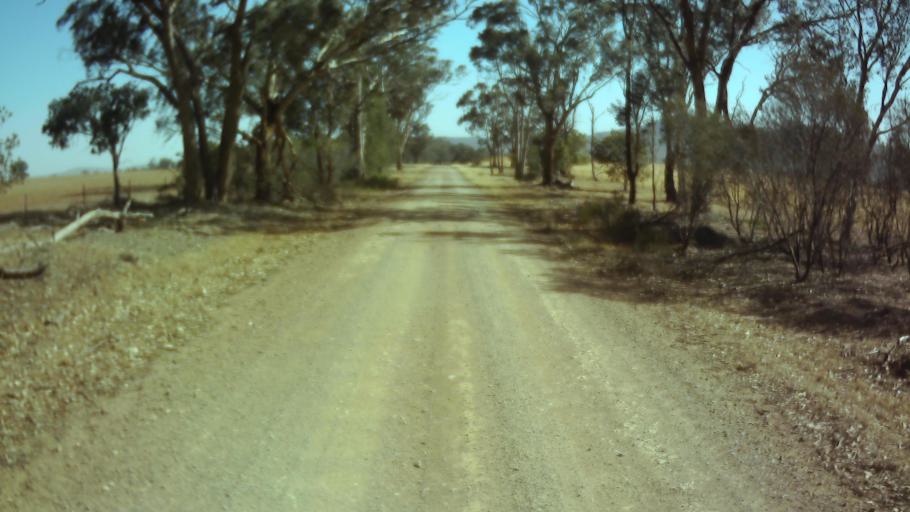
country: AU
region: New South Wales
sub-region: Weddin
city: Grenfell
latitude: -33.8506
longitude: 148.0165
